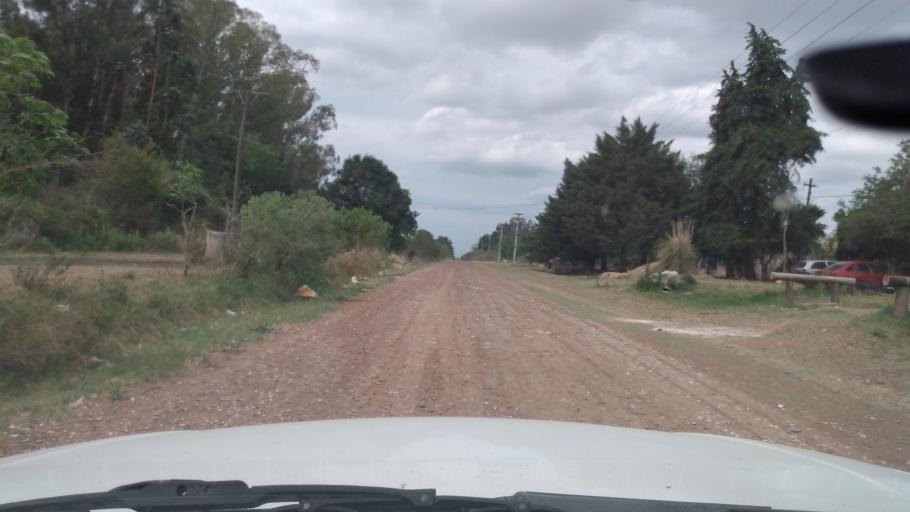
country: AR
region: Buenos Aires
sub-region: Partido de Lujan
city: Lujan
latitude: -34.5601
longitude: -59.1869
